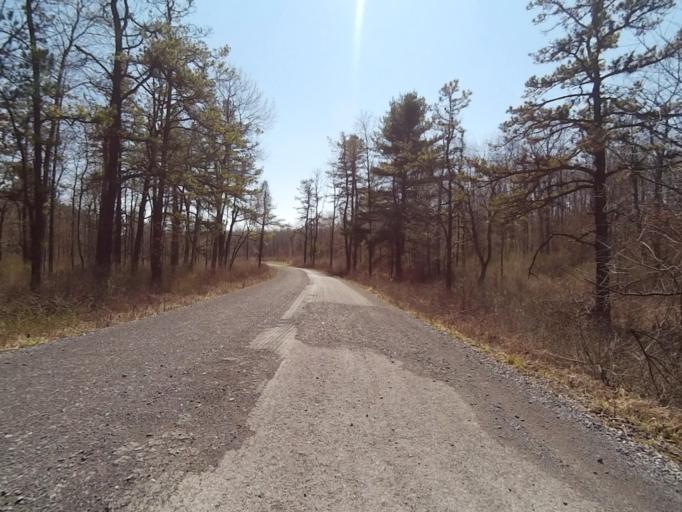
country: US
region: Pennsylvania
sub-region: Centre County
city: Park Forest Village
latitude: 40.7895
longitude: -77.9513
